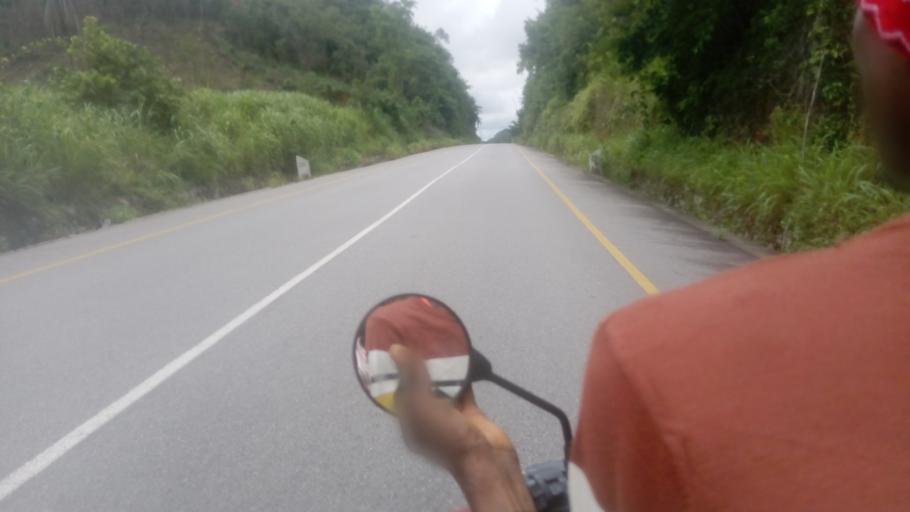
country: SL
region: Northern Province
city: Masaka
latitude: 8.6451
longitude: -11.7462
